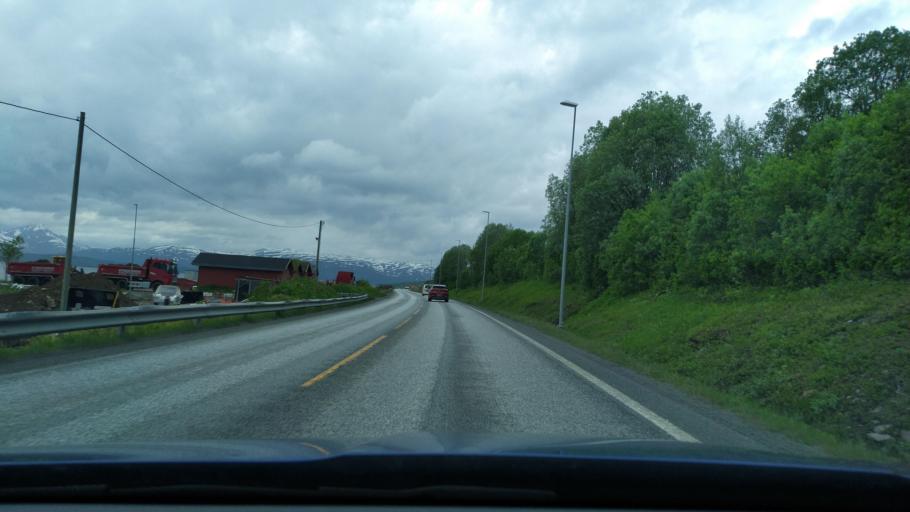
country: NO
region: Troms
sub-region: Tromso
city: Tromso
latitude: 69.5951
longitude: 18.9383
